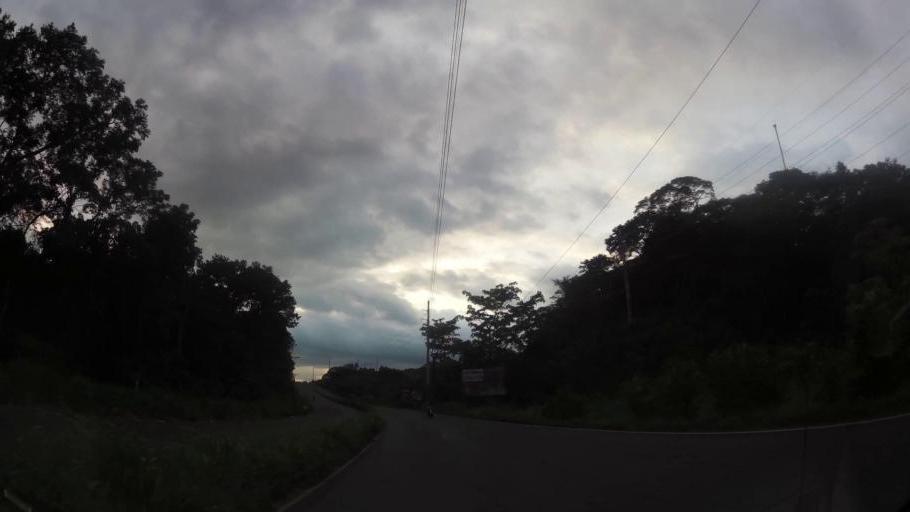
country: GT
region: Suchitepeque
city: Patulul
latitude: 14.3640
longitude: -91.0985
